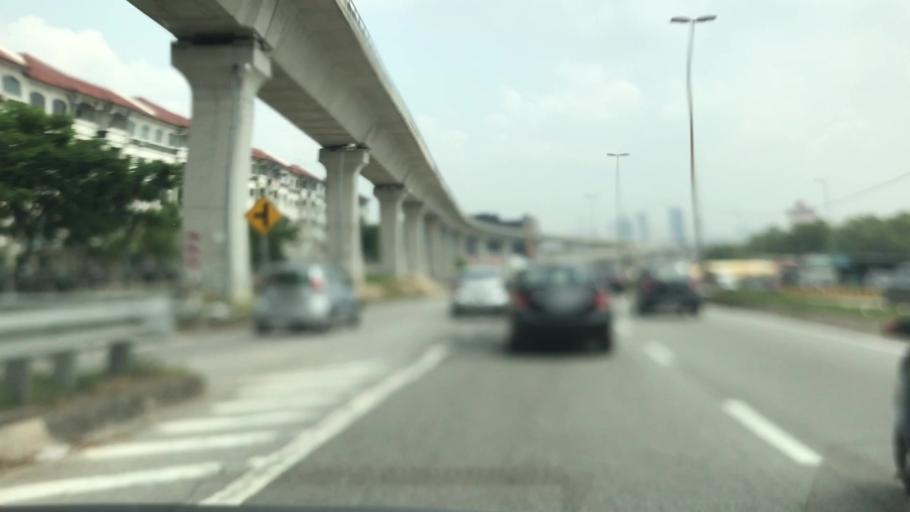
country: MY
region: Selangor
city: Subang Jaya
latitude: 3.0498
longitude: 101.6281
